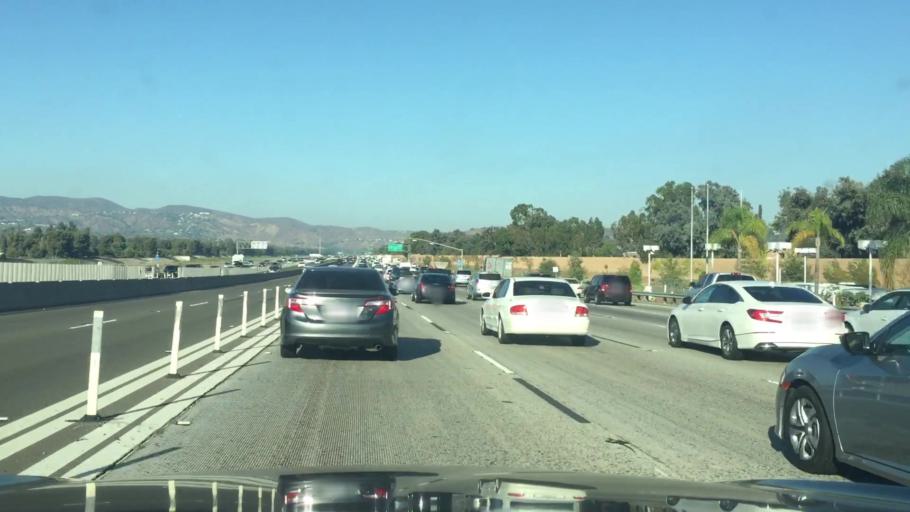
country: US
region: California
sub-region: Orange County
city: Yorba Linda
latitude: 33.8572
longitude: -117.7852
